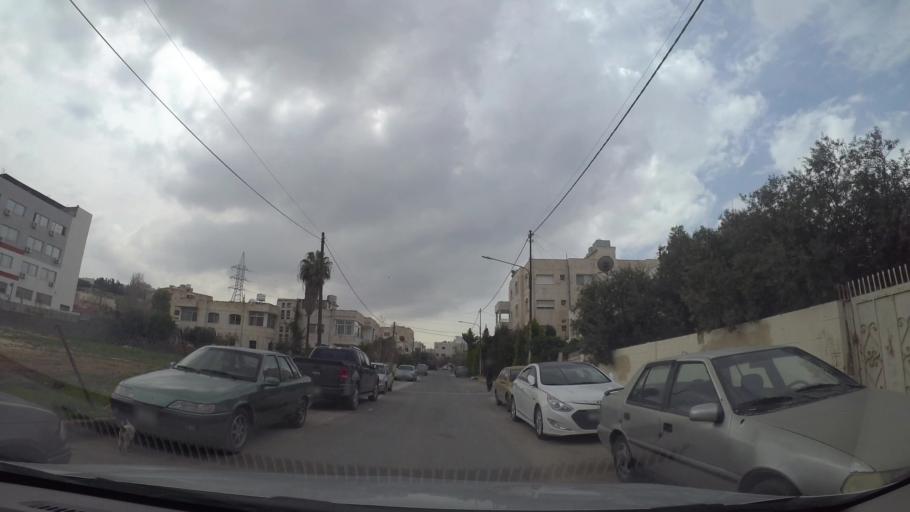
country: JO
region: Amman
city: Umm as Summaq
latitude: 31.8933
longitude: 35.8405
